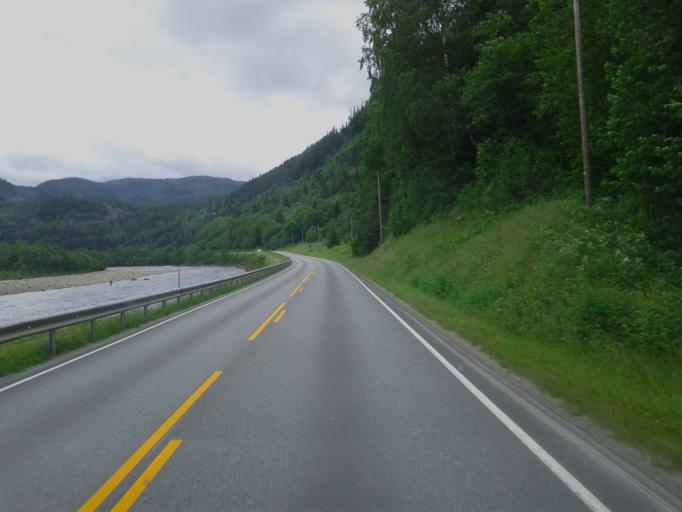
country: NO
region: Sor-Trondelag
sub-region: Midtre Gauldal
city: Storen
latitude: 62.9599
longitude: 10.5861
